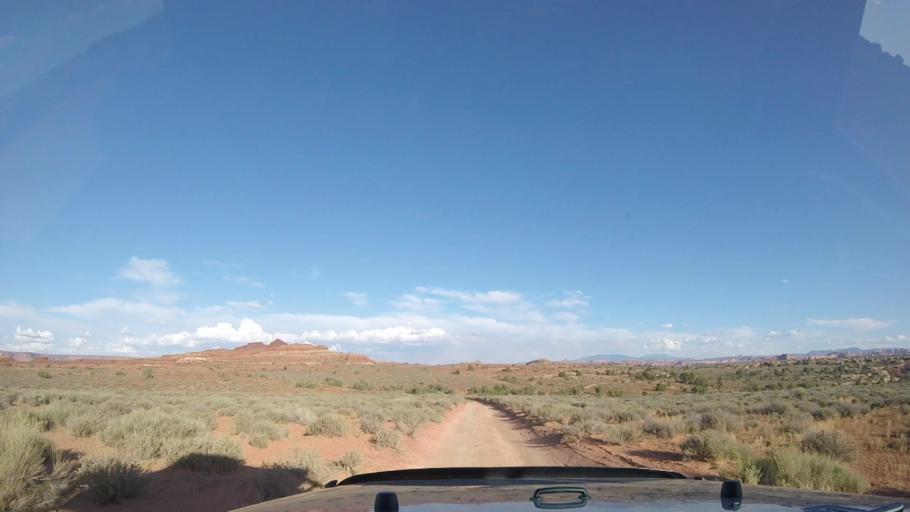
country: US
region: Utah
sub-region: Grand County
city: Moab
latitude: 38.2125
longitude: -109.7892
